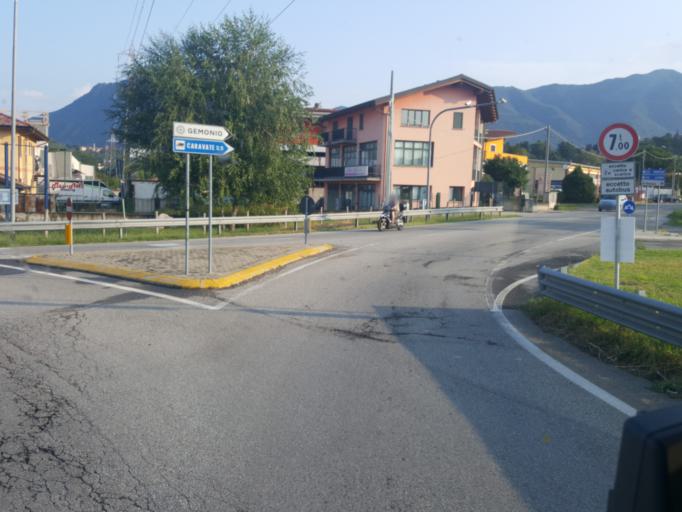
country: IT
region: Lombardy
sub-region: Provincia di Varese
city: Gemonio
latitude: 45.8708
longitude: 8.6725
